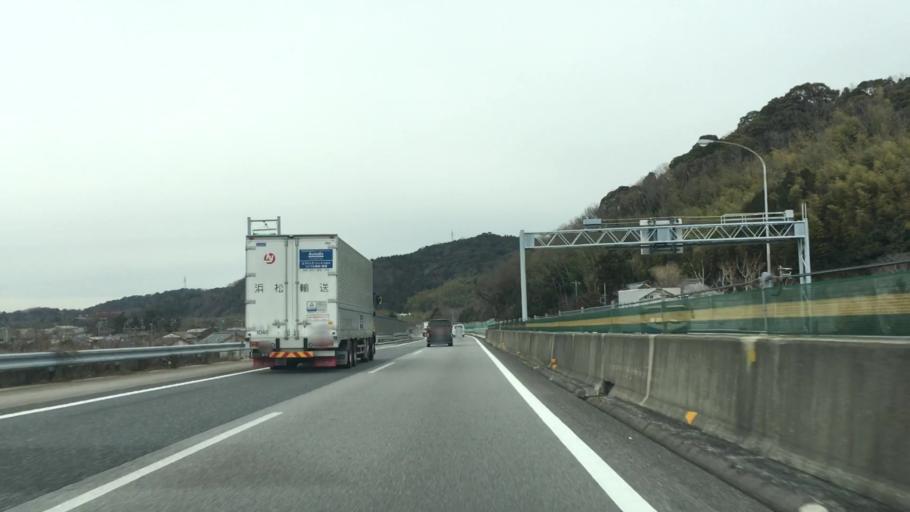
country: JP
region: Aichi
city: Okazaki
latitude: 34.9281
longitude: 137.2229
